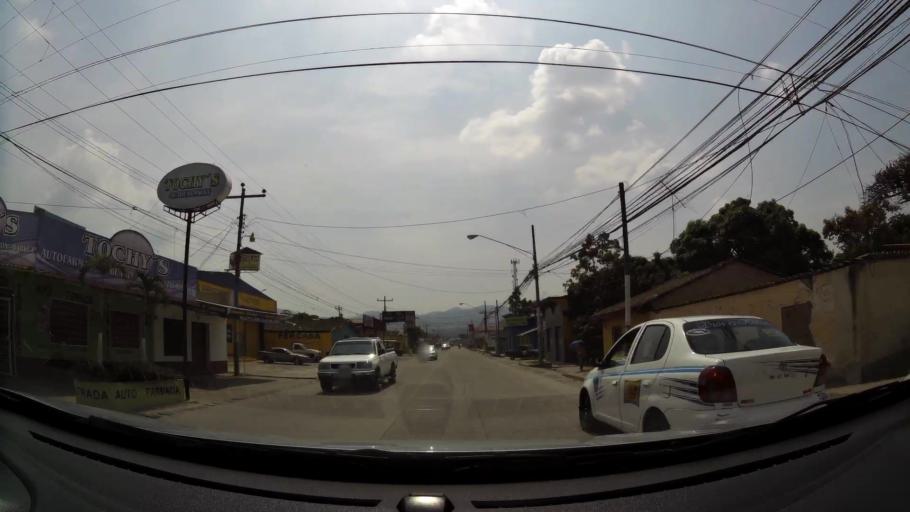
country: HN
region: Comayagua
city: Siguatepeque
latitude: 14.5971
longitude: -87.8381
